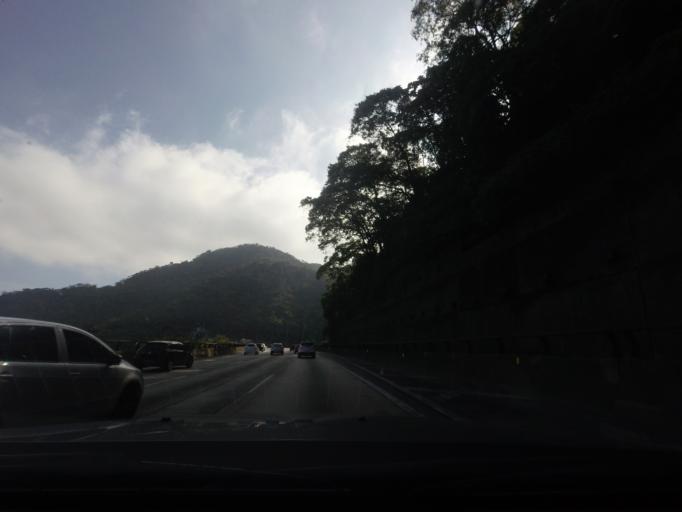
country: BR
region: Sao Paulo
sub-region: Cubatao
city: Cubatao
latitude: -23.9082
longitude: -46.5154
